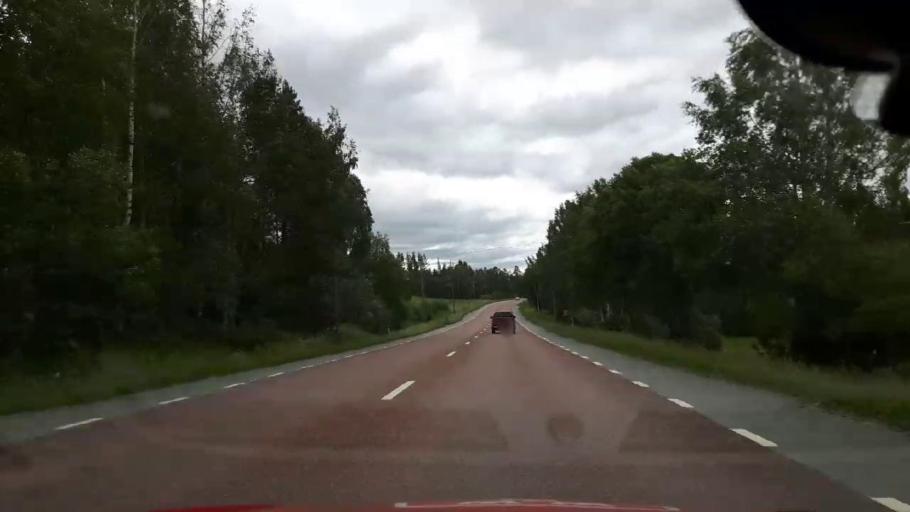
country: SE
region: Jaemtland
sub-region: Braecke Kommun
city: Braecke
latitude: 62.7862
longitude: 15.3820
